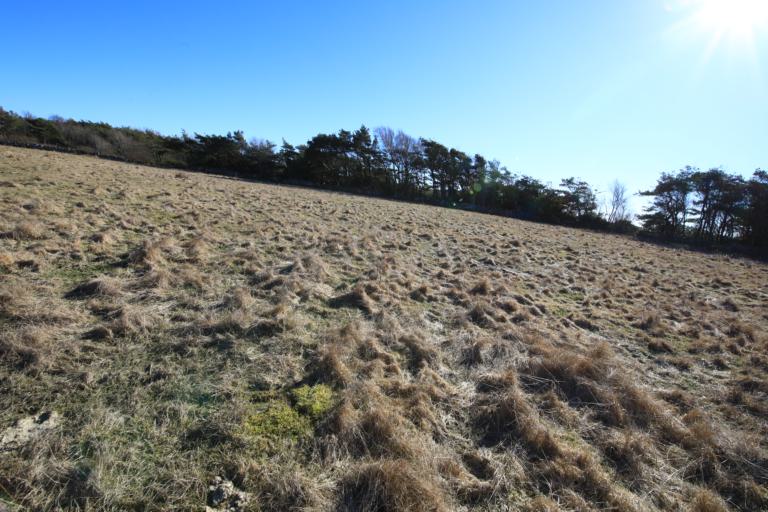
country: SE
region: Halland
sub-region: Kungsbacka Kommun
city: Frillesas
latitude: 57.2258
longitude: 12.1283
